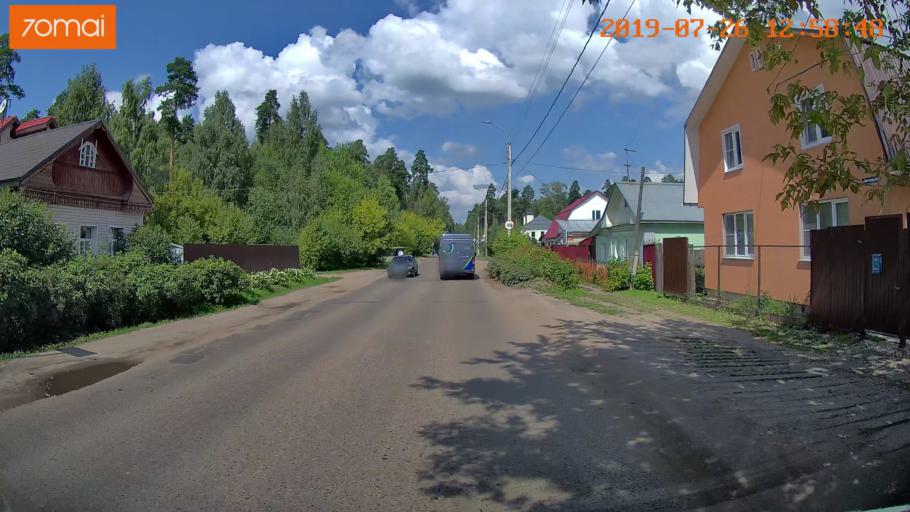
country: RU
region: Ivanovo
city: Bogorodskoye
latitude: 57.0258
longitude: 41.0208
